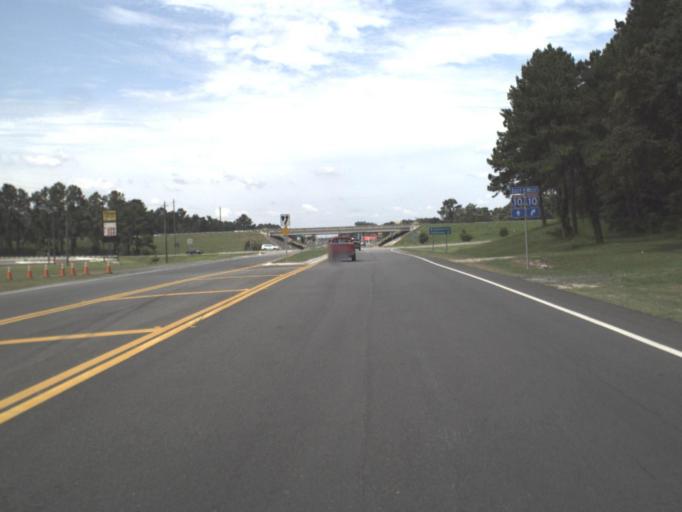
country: US
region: Florida
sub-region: Suwannee County
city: Live Oak
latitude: 30.3333
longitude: -82.9607
